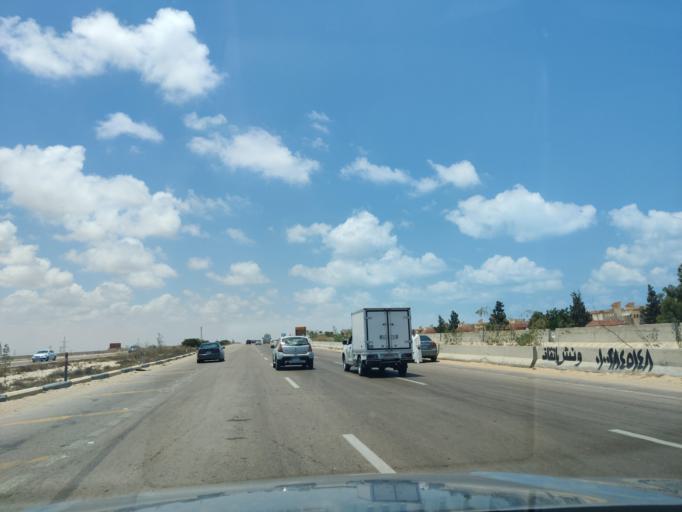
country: EG
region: Muhafazat Matruh
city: Al `Alamayn
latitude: 30.8311
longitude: 29.2187
